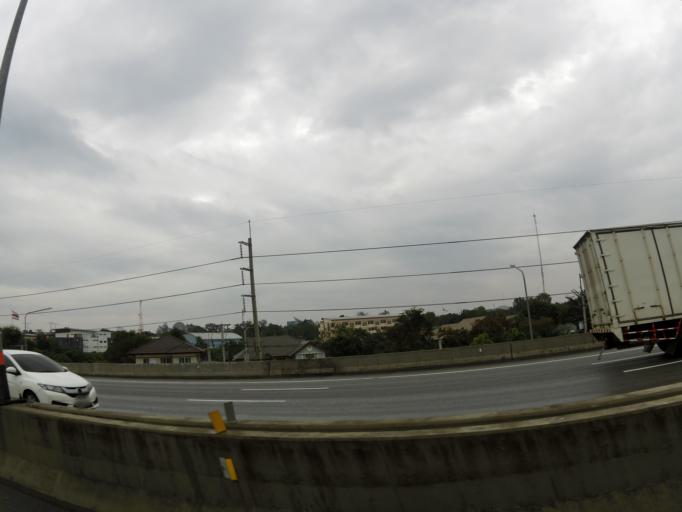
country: TH
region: Chon Buri
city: Bang Lamung
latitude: 13.1080
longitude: 100.9253
